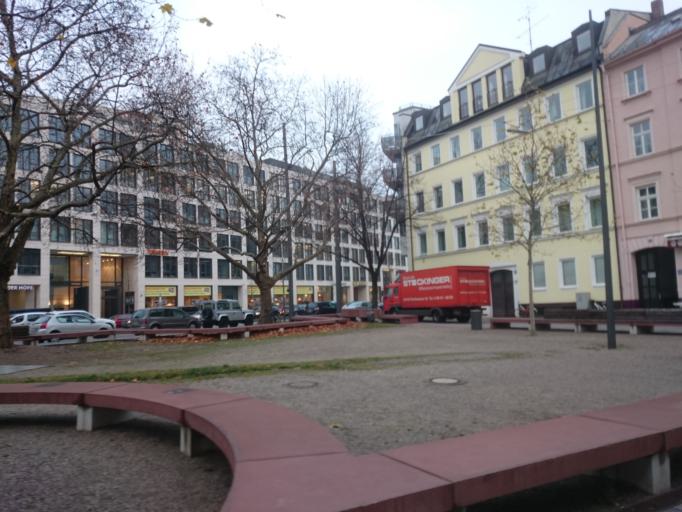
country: DE
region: Bavaria
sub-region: Upper Bavaria
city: Munich
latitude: 48.1487
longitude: 11.5591
